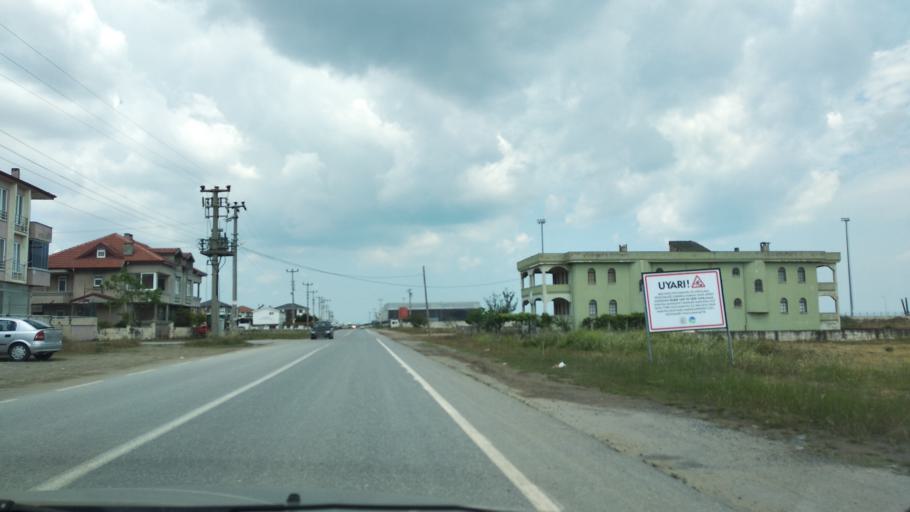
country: TR
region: Sakarya
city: Karasu
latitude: 41.1154
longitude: 30.6784
